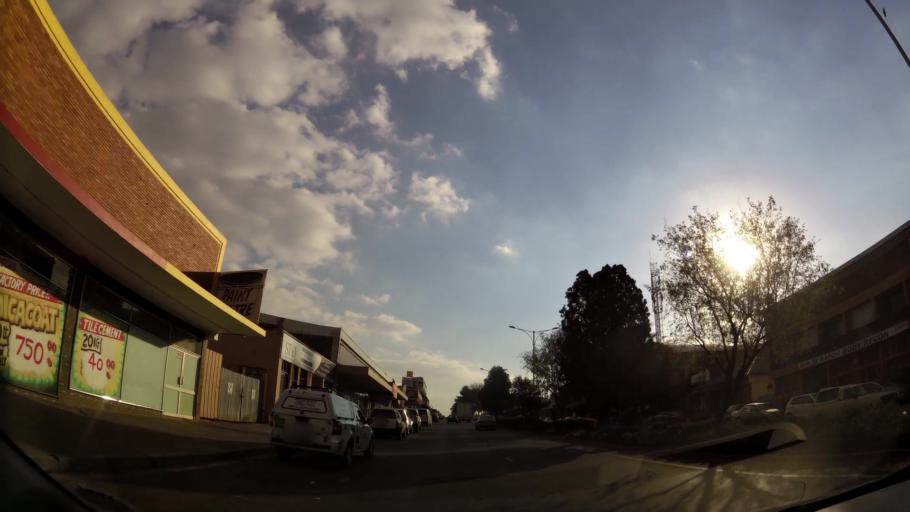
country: ZA
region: Gauteng
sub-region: West Rand District Municipality
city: Krugersdorp
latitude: -26.0981
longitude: 27.7509
